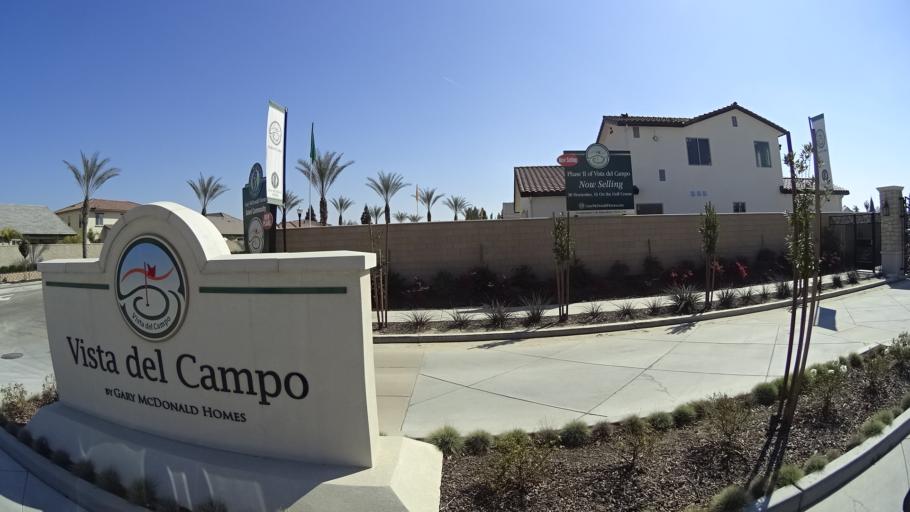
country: US
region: California
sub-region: Fresno County
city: Clovis
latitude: 36.9083
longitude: -119.7449
